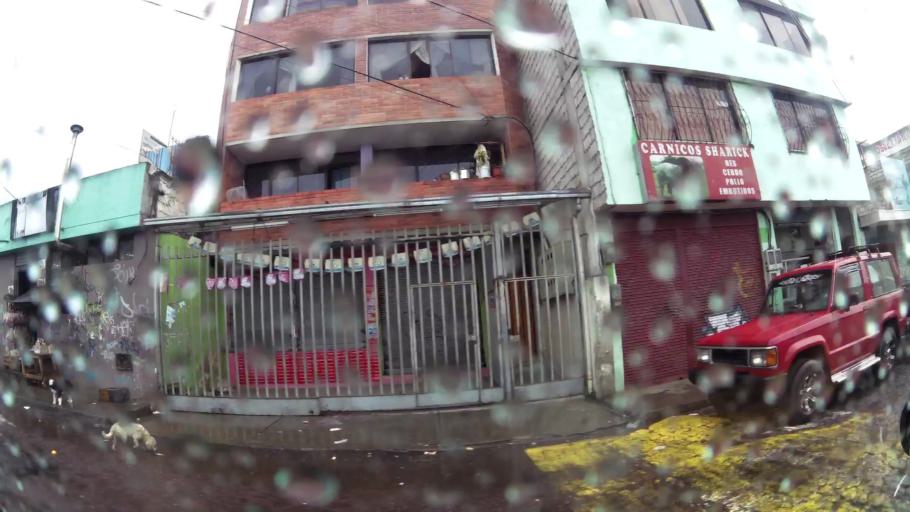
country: EC
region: Pichincha
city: Quito
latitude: -0.0852
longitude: -78.5098
